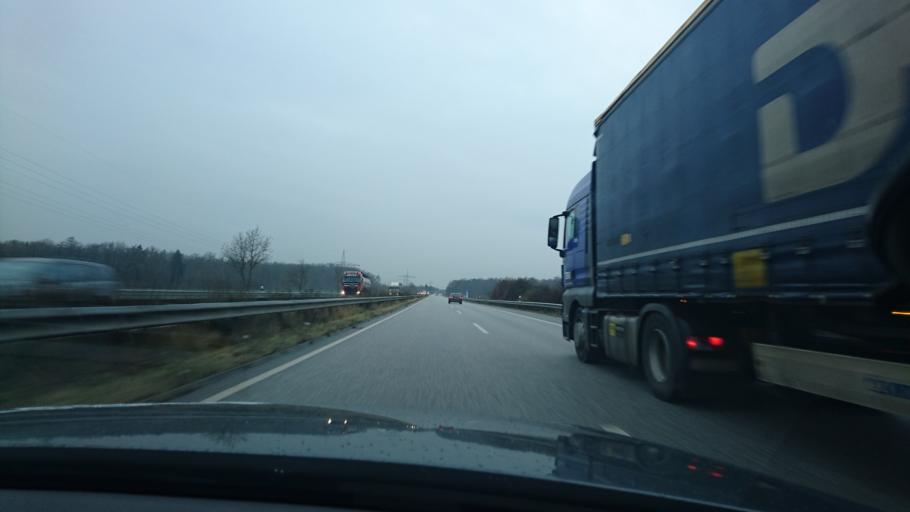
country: DE
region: Schleswig-Holstein
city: Lensahn
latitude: 54.2315
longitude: 10.8972
